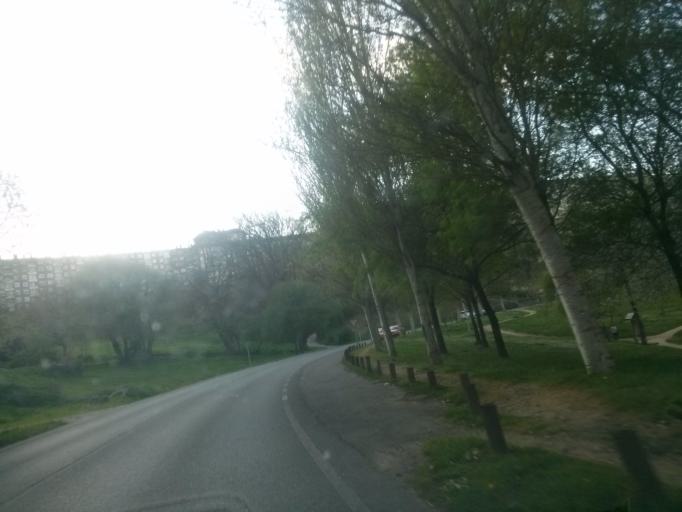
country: ES
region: Galicia
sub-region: Provincia de Lugo
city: Lugo
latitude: 43.0068
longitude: -7.5458
